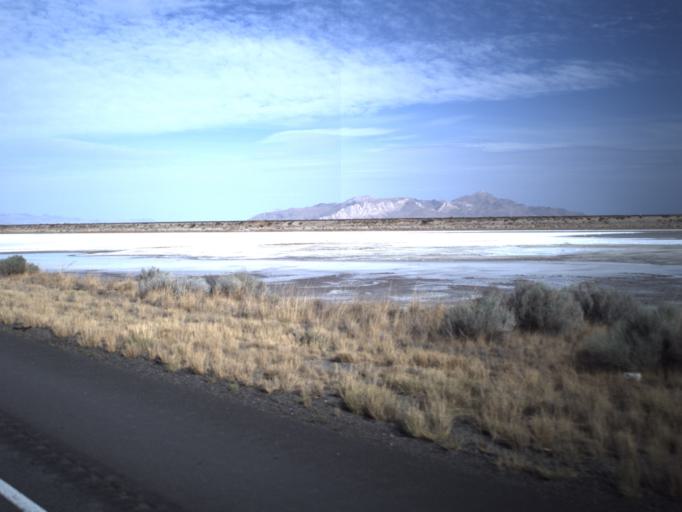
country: US
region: Utah
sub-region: Tooele County
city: Stansbury park
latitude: 40.6649
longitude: -112.3627
